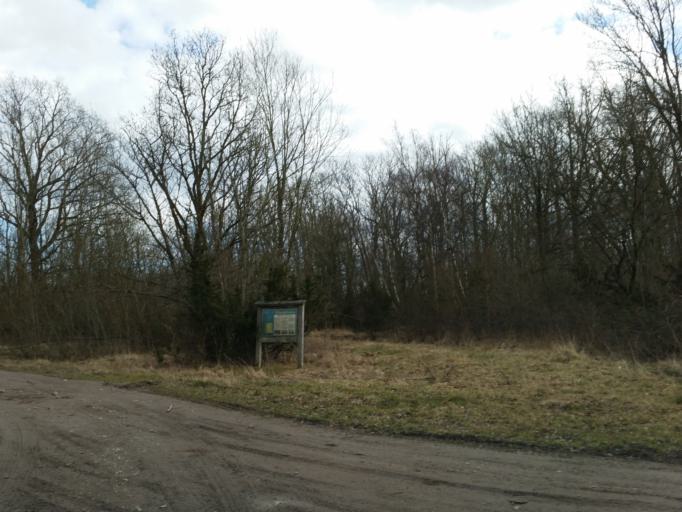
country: SE
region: Kalmar
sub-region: Morbylanga Kommun
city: Sodra Sandby
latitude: 56.6737
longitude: 16.6368
